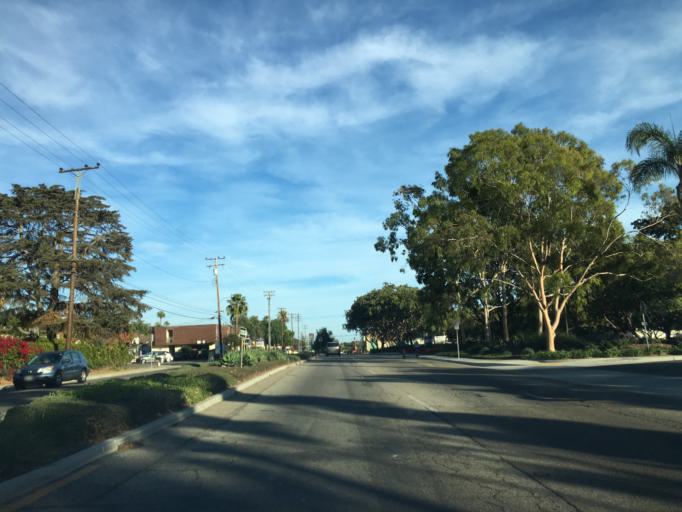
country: US
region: California
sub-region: Santa Barbara County
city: Goleta
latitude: 34.4351
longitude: -119.8135
